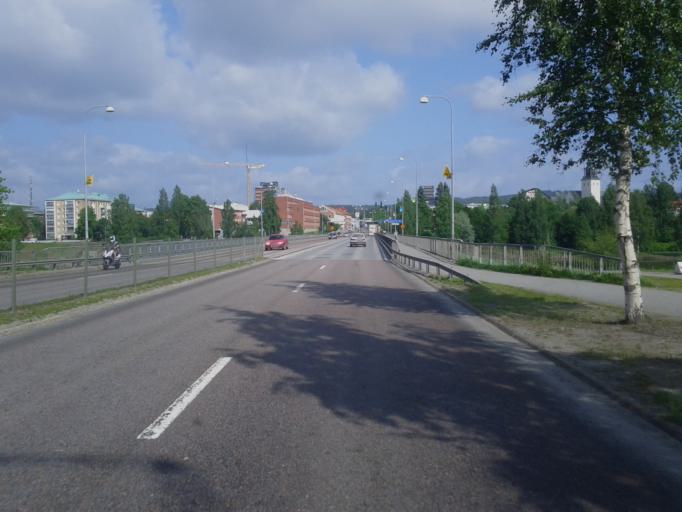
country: SE
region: Vaesterbotten
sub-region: Skelleftea Kommun
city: Skelleftea
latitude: 64.7459
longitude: 20.9597
